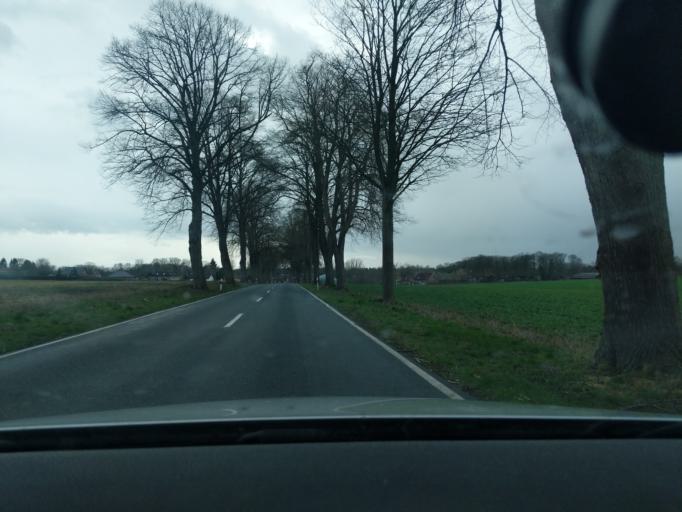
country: DE
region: Lower Saxony
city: Bliedersdorf
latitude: 53.4909
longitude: 9.5259
